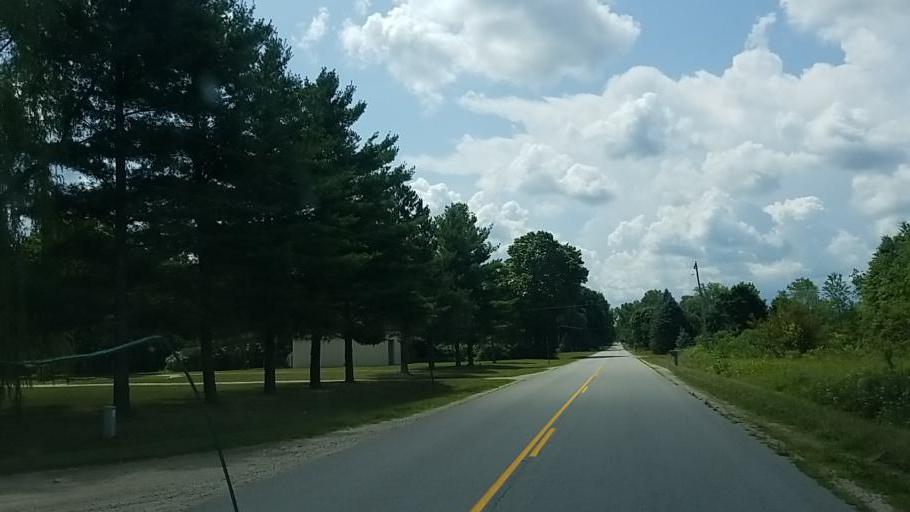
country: US
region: Michigan
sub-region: Muskegon County
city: Ravenna
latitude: 43.2035
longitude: -85.8794
